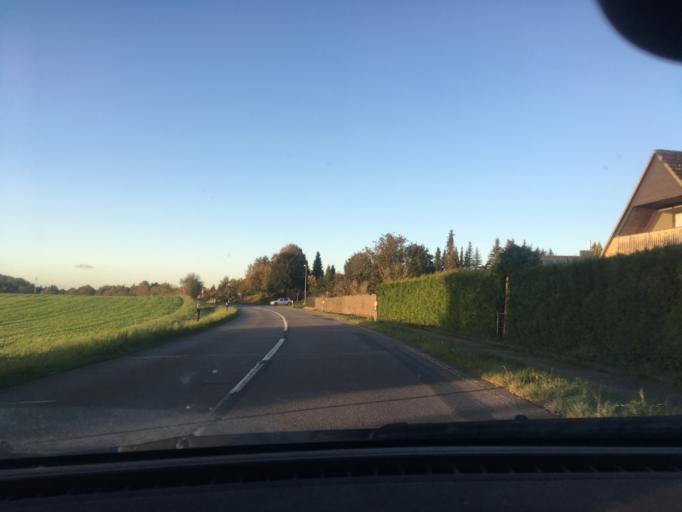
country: DE
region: Lower Saxony
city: Wendisch Evern
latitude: 53.2118
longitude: 10.4656
